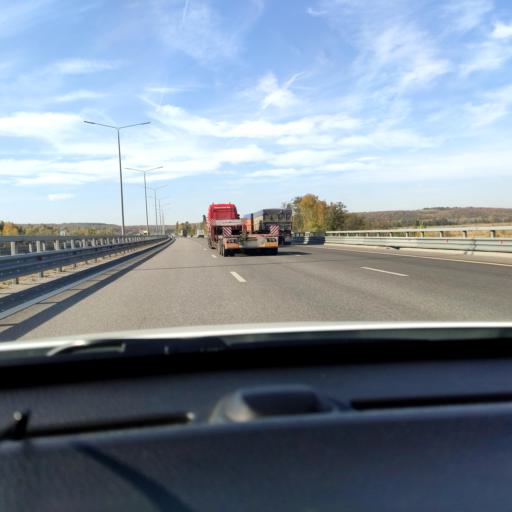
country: RU
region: Voronezj
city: Somovo
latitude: 51.7880
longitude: 39.2823
